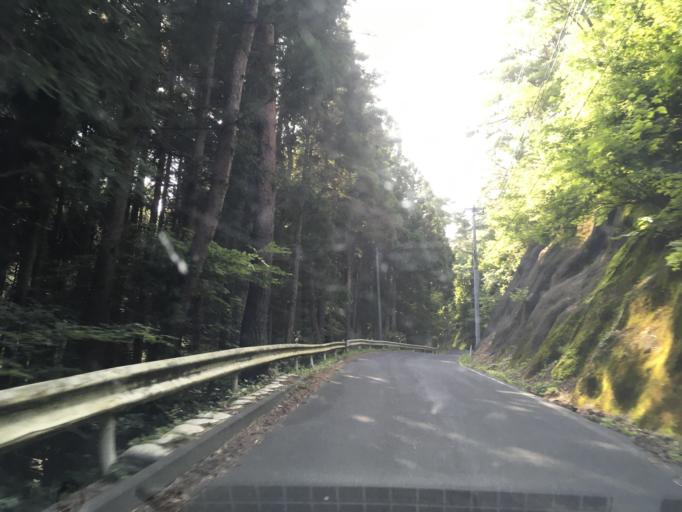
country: JP
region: Iwate
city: Ofunato
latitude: 38.9151
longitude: 141.6160
